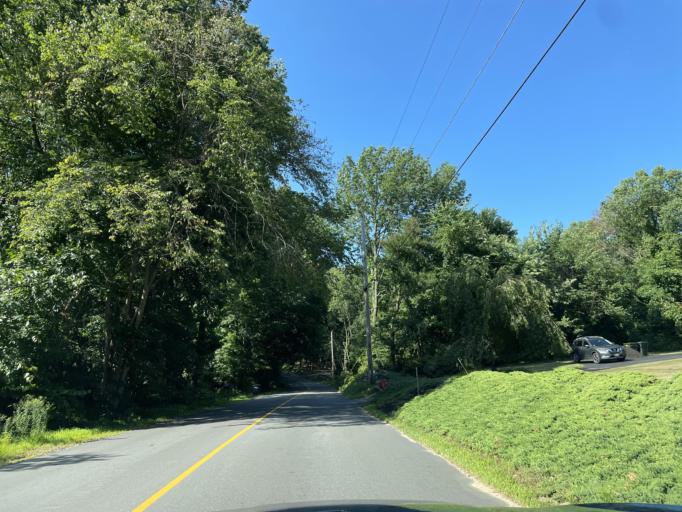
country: US
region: Massachusetts
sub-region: Worcester County
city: Charlton
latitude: 42.1358
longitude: -71.9415
